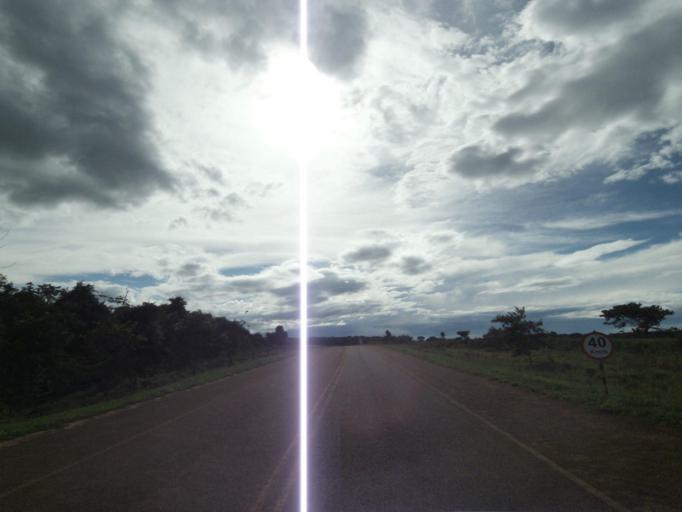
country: BR
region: Goias
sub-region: Jaragua
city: Jaragua
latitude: -15.8420
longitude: -49.3538
